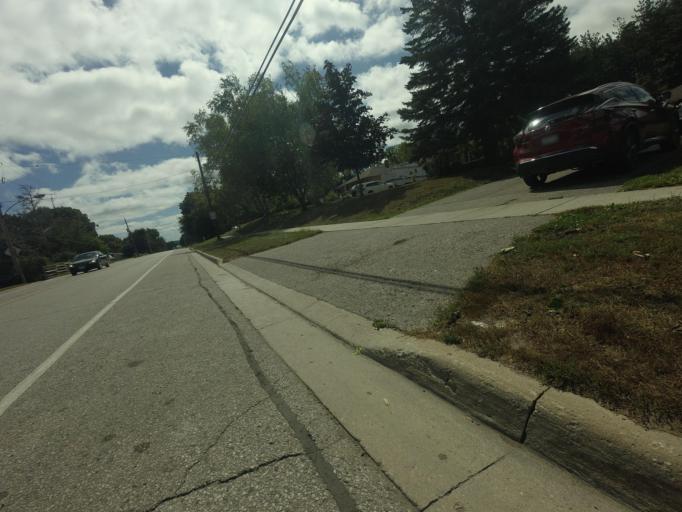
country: CA
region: Ontario
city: Uxbridge
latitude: 44.1232
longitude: -79.1267
